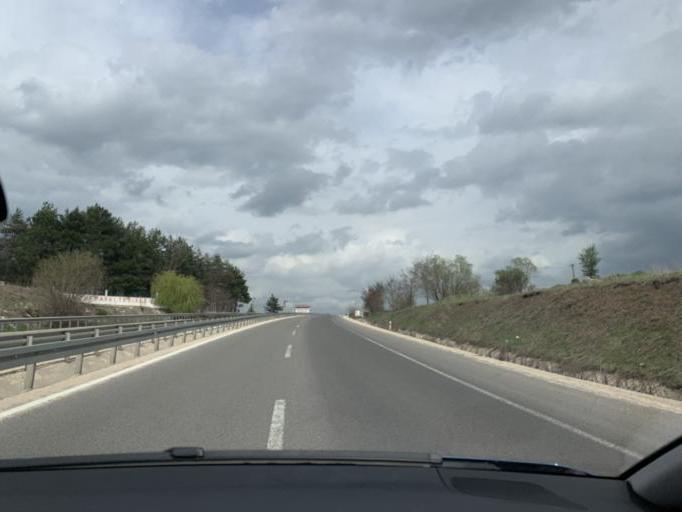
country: TR
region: Bolu
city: Yenicaga
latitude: 40.7824
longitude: 32.0758
